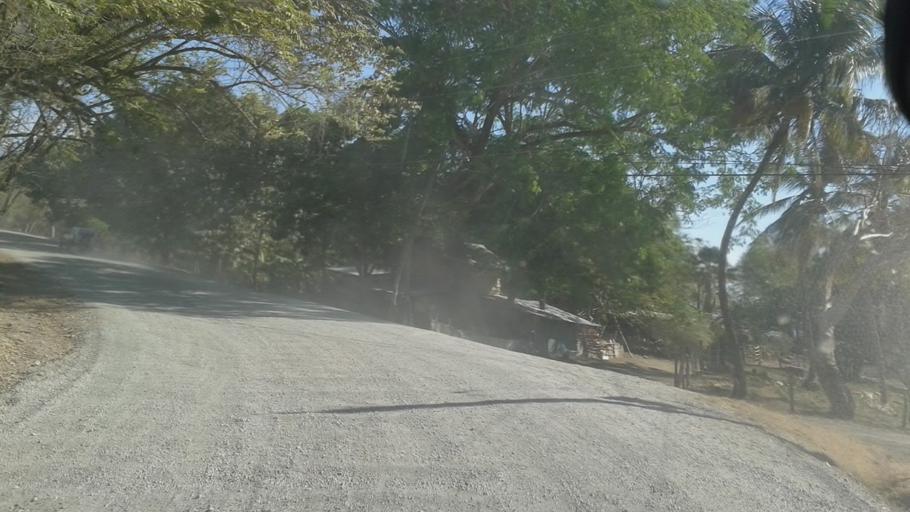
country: CR
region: Guanacaste
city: Santa Cruz
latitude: 10.1258
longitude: -85.7947
